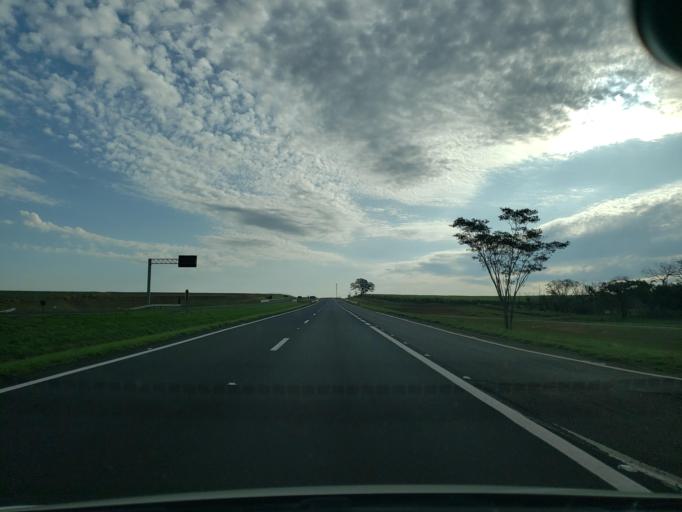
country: BR
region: Sao Paulo
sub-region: Valparaiso
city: Valparaiso
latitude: -21.2076
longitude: -50.7535
